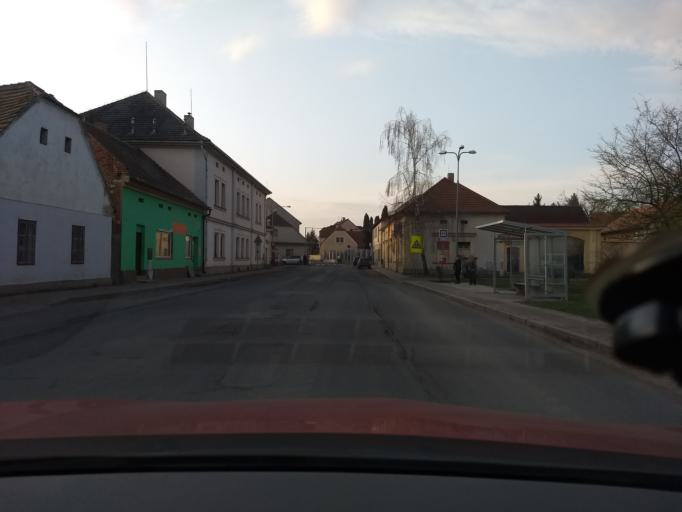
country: CZ
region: Central Bohemia
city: Rudna
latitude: 50.0424
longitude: 14.1863
